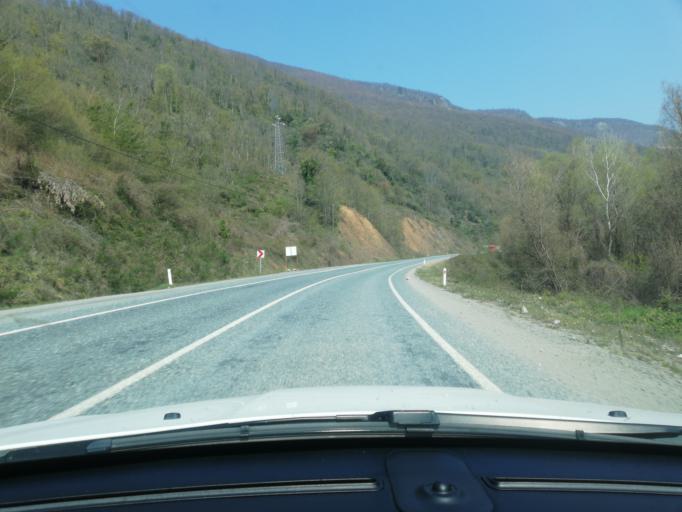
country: TR
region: Zonguldak
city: Gokcebey
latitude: 41.2654
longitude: 32.1590
